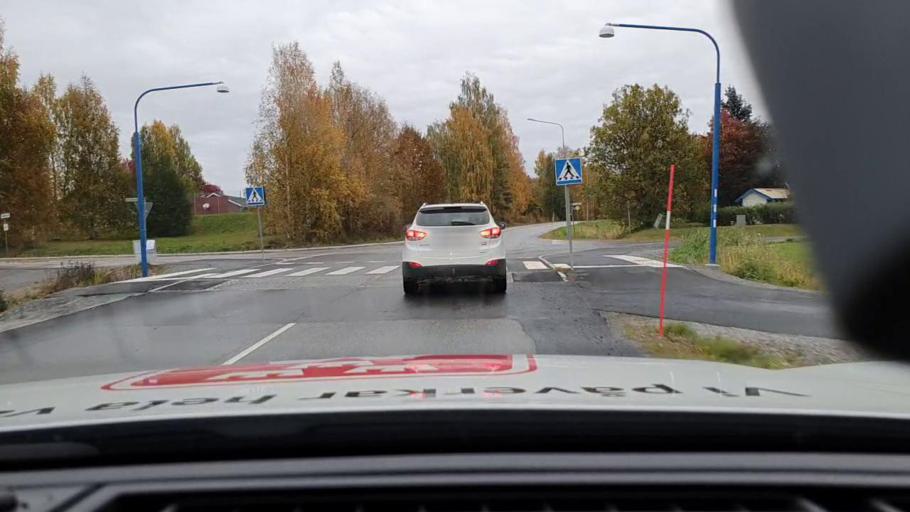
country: SE
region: Norrbotten
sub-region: Bodens Kommun
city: Saevast
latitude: 65.7696
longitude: 21.7244
